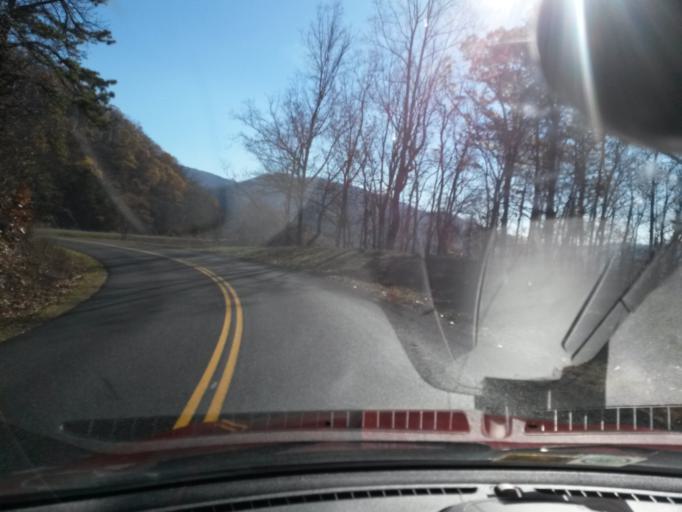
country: US
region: Virginia
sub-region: Botetourt County
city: Buchanan
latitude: 37.4780
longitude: -79.6534
